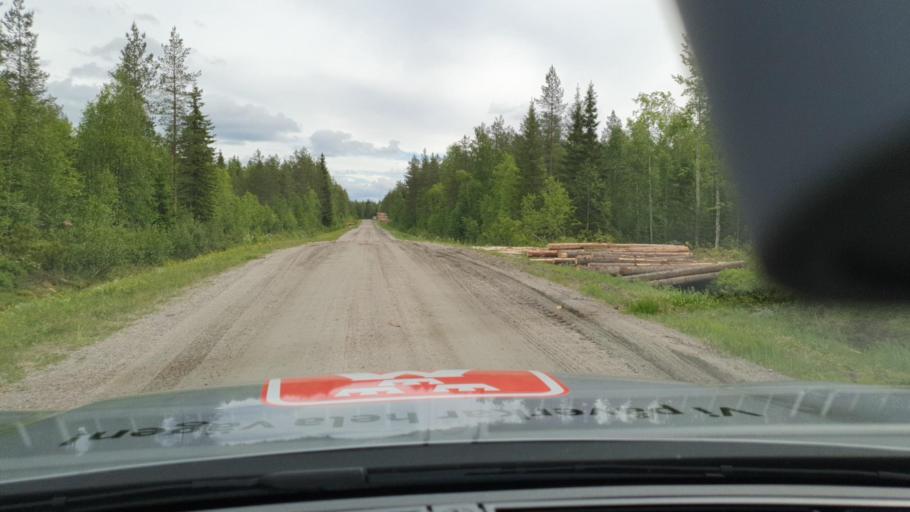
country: FI
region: Lapland
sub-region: Torniolaakso
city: Ylitornio
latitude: 65.9530
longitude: 23.5886
